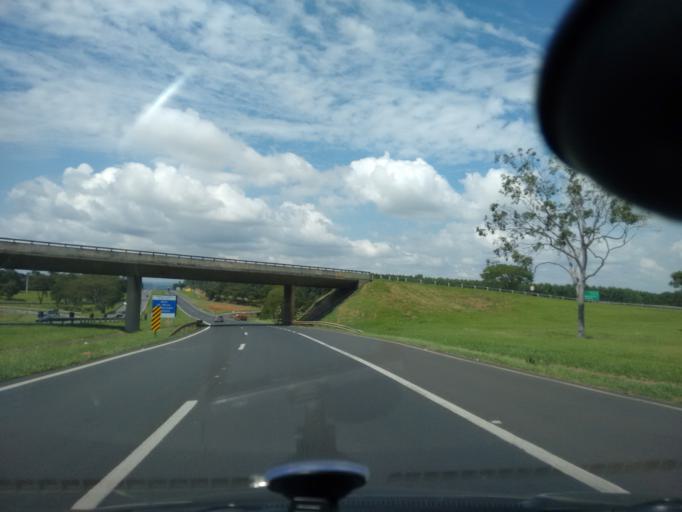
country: BR
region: Sao Paulo
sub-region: Sao Carlos
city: Sao Carlos
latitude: -22.0451
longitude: -47.8619
